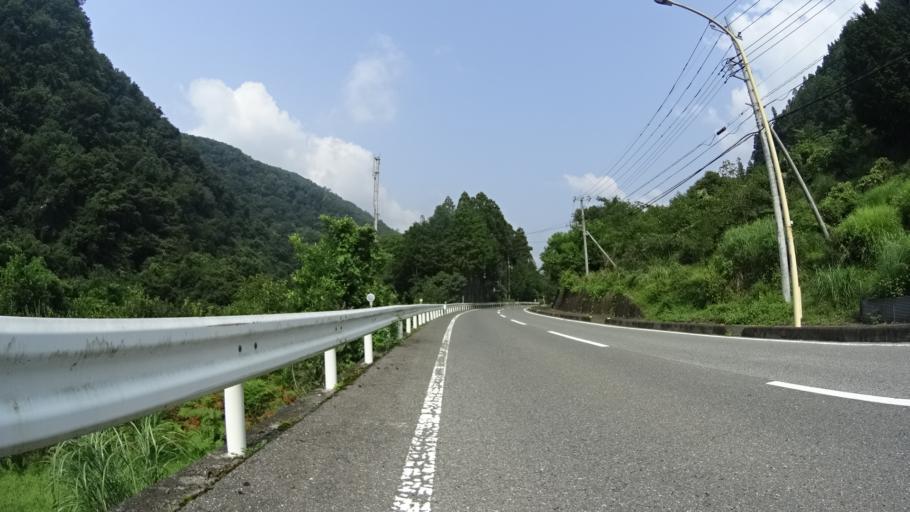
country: JP
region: Saitama
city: Chichibu
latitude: 36.0354
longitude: 138.9199
